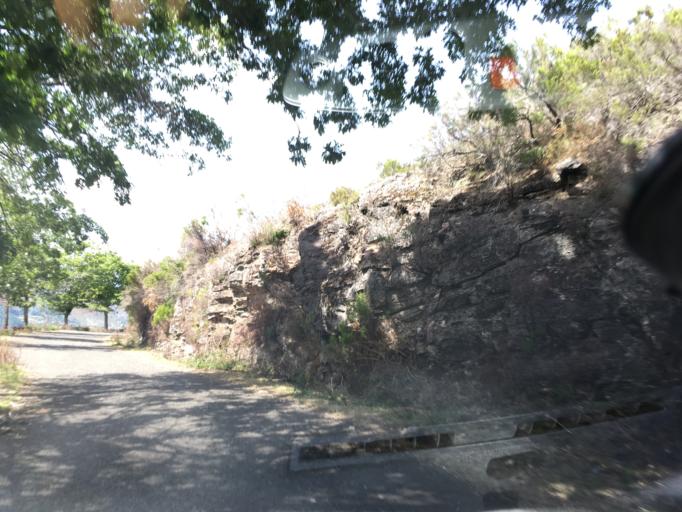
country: PT
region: Braga
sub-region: Celorico de Basto
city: Celorico de Basto
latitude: 41.2811
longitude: -7.9416
